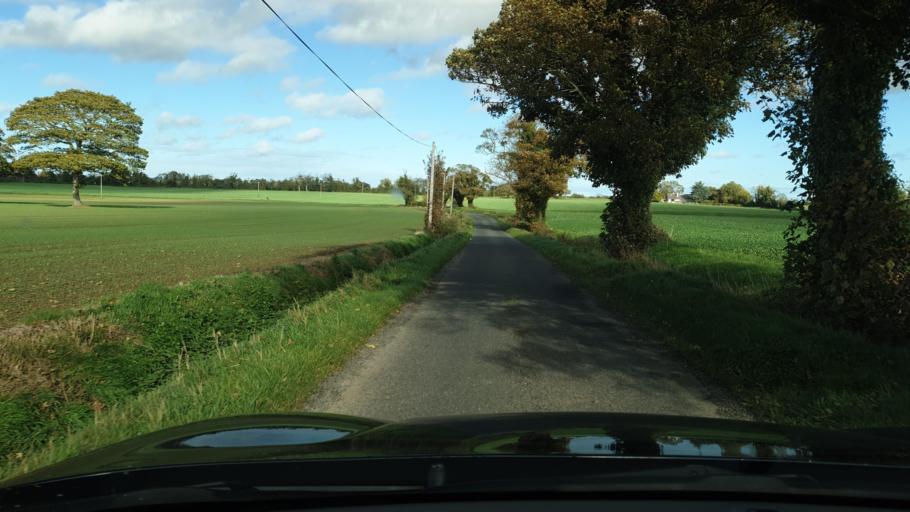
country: IE
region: Leinster
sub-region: Fingal County
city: Swords
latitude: 53.4987
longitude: -6.2426
